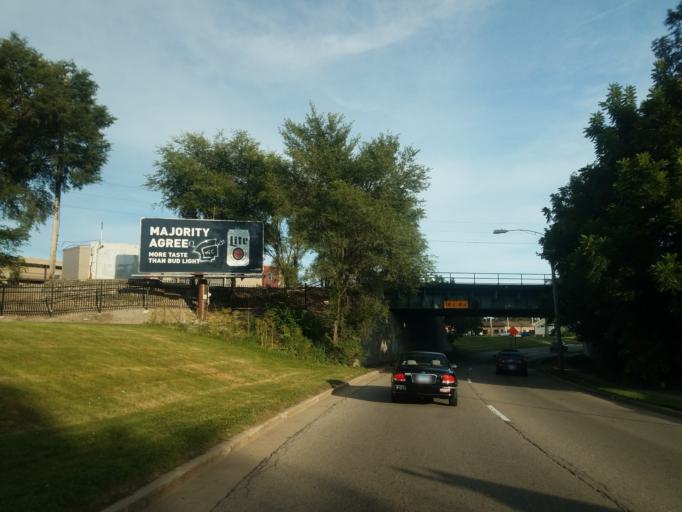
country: US
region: Illinois
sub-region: McLean County
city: Normal
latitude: 40.5018
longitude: -88.9954
